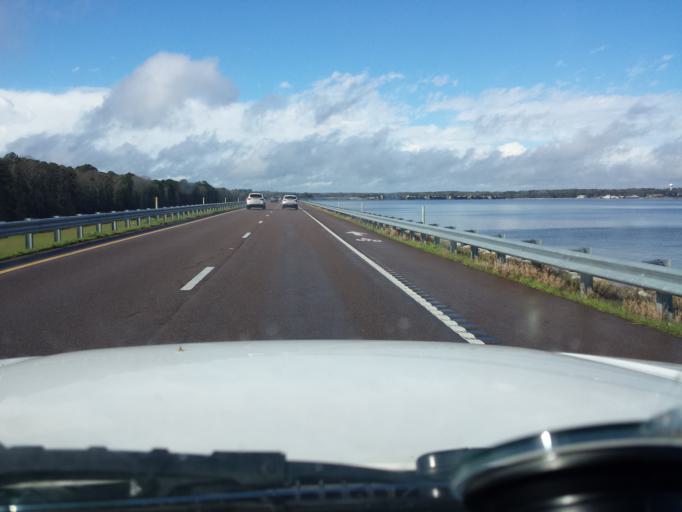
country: US
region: Mississippi
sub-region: Madison County
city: Ridgeland
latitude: 32.4041
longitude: -90.0748
